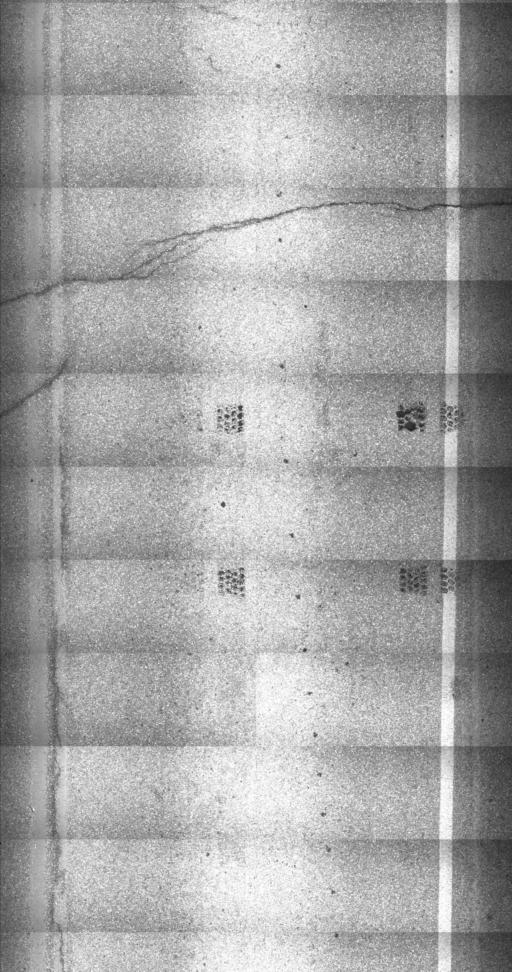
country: US
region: Vermont
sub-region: Franklin County
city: Enosburg Falls
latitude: 44.7858
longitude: -72.8006
